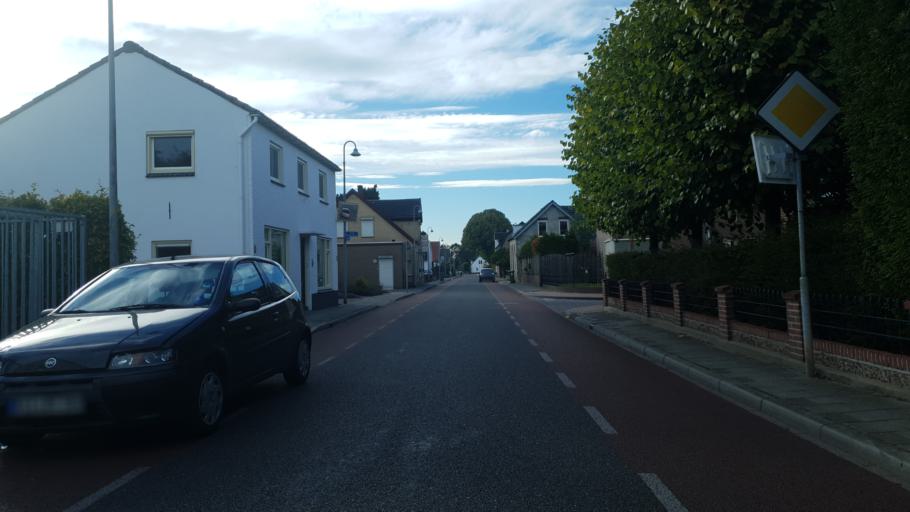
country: NL
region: Gelderland
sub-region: Gemeente Zevenaar
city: Zevenaar
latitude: 51.8602
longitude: 6.0589
